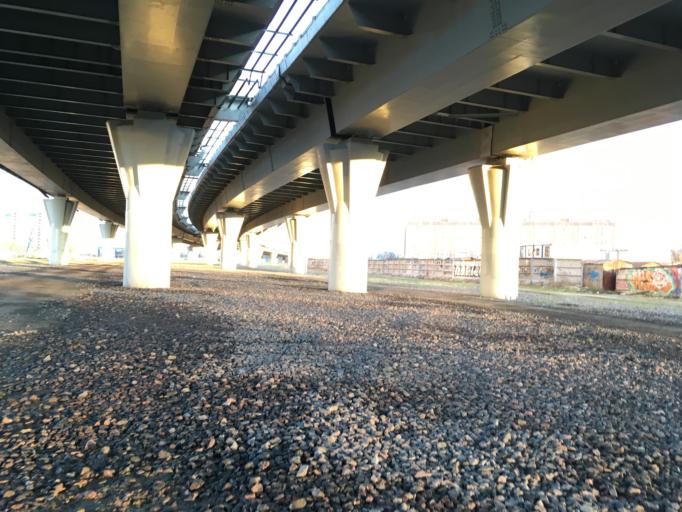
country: RU
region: Leningrad
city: Untolovo
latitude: 60.0112
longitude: 30.2321
